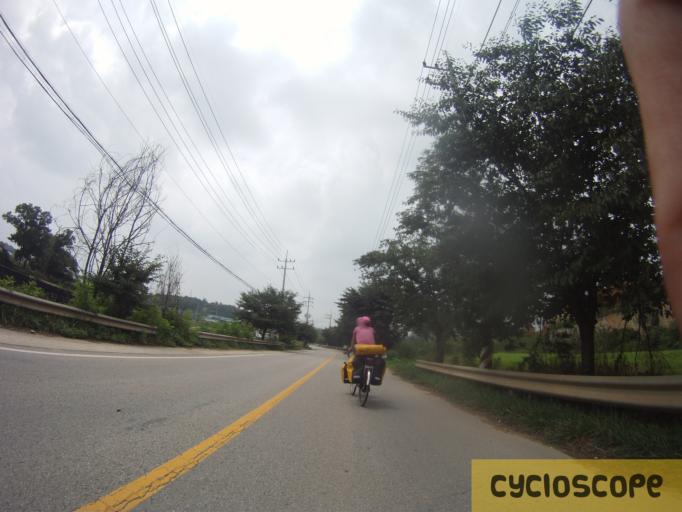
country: KR
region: Gyeonggi-do
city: Hwaseong-si
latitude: 37.1389
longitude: 126.8632
